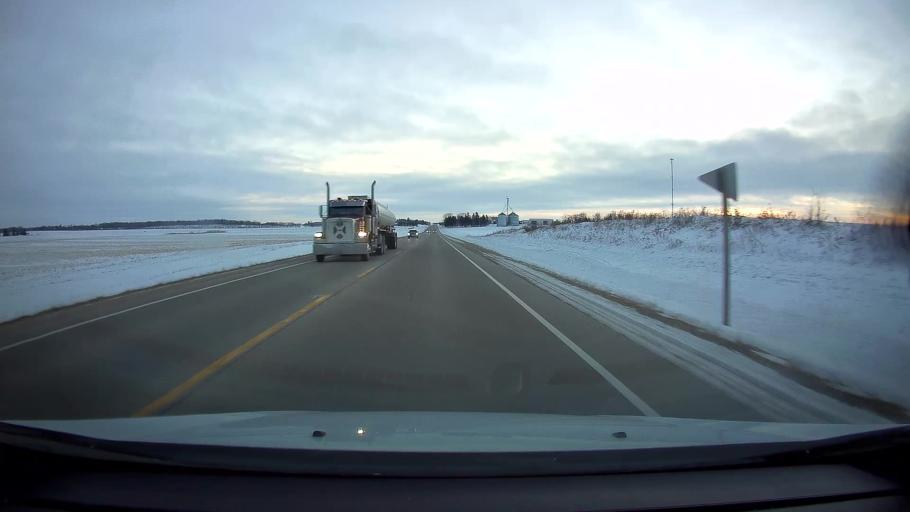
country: US
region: Wisconsin
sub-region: Saint Croix County
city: New Richmond
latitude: 45.1365
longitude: -92.4765
